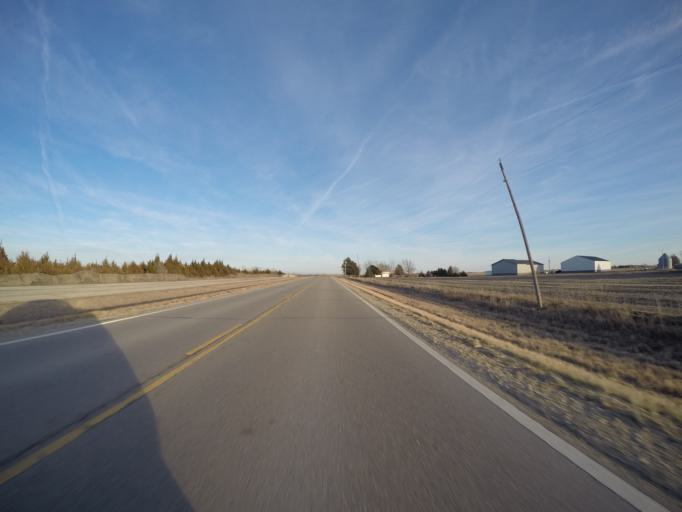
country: US
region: Kansas
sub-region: Dickinson County
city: Herington
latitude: 38.6642
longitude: -96.8744
